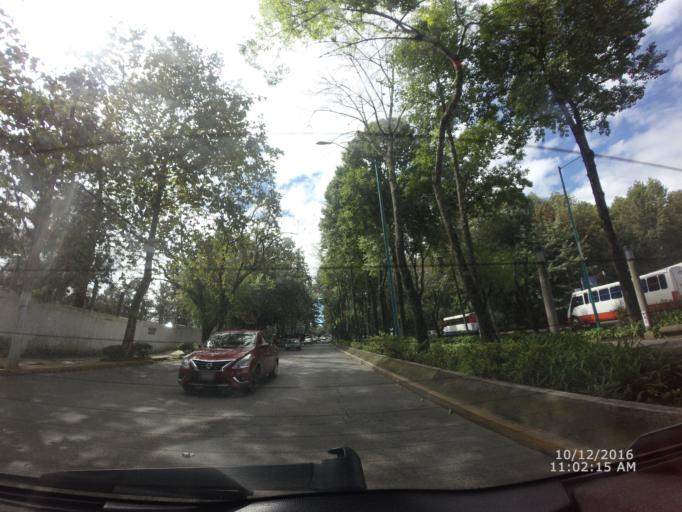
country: TR
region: Sivas
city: Karayun
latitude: 39.6722
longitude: 37.2363
